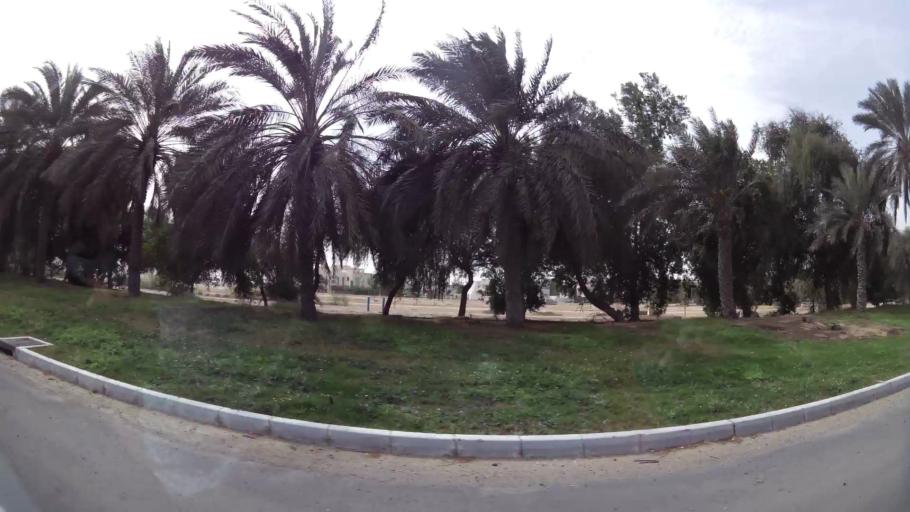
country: AE
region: Abu Dhabi
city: Abu Dhabi
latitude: 24.3941
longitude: 54.5184
